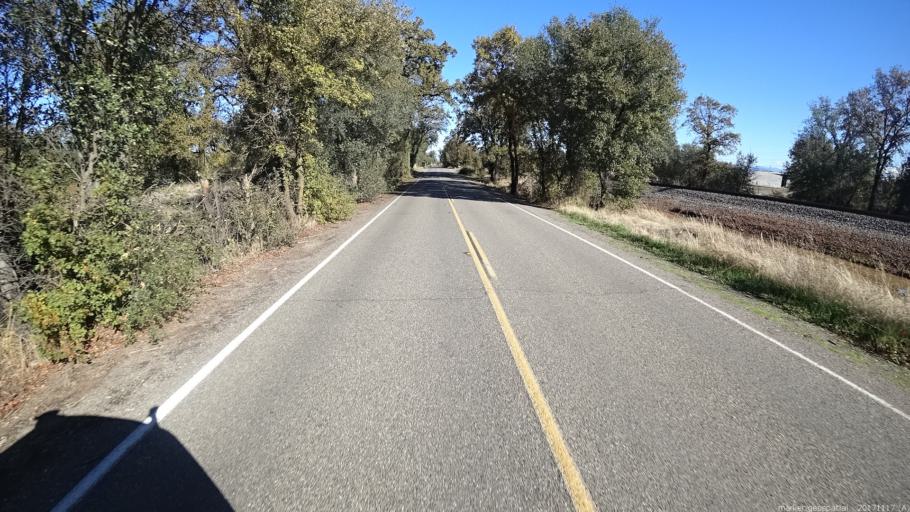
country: US
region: California
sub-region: Shasta County
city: Cottonwood
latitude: 40.3864
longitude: -122.2726
